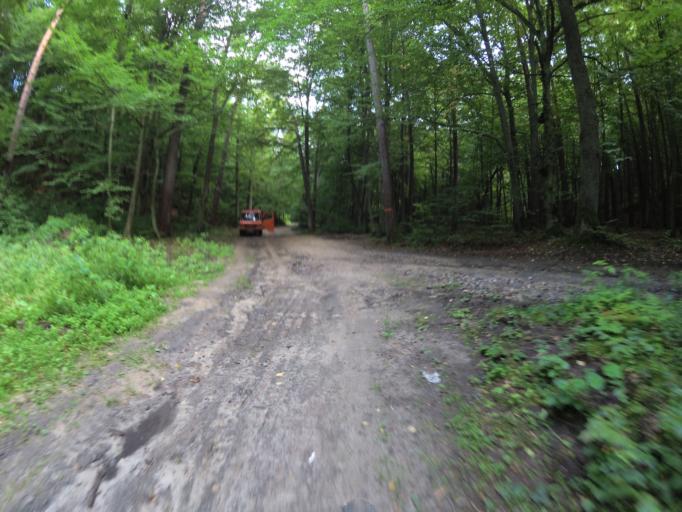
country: PL
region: Pomeranian Voivodeship
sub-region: Gdynia
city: Wielki Kack
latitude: 54.4892
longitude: 18.4528
